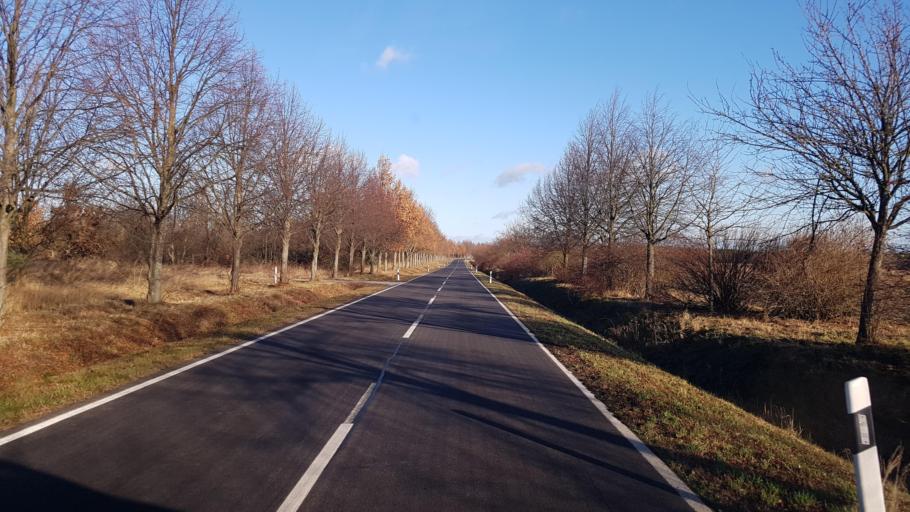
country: DE
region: Brandenburg
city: Forst
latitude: 51.7614
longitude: 14.5665
